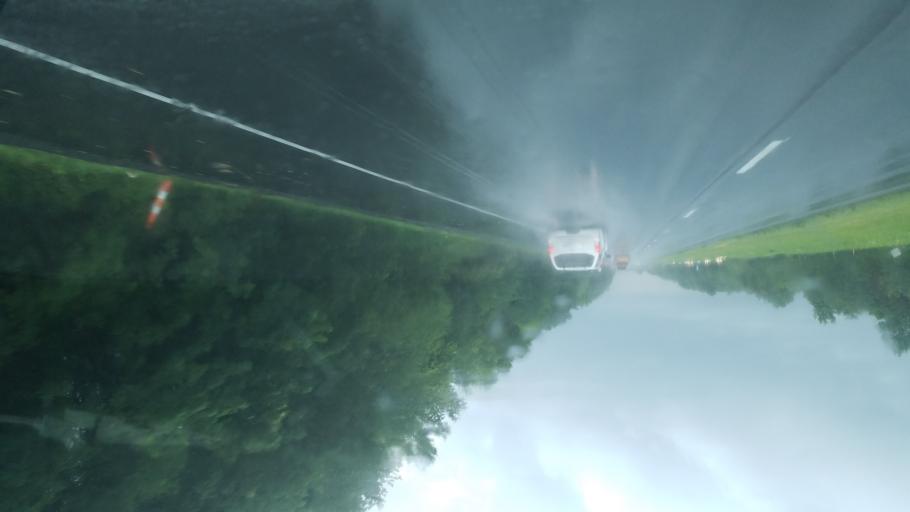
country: US
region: Ohio
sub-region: Trumbull County
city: Churchill
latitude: 41.1796
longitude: -80.6869
